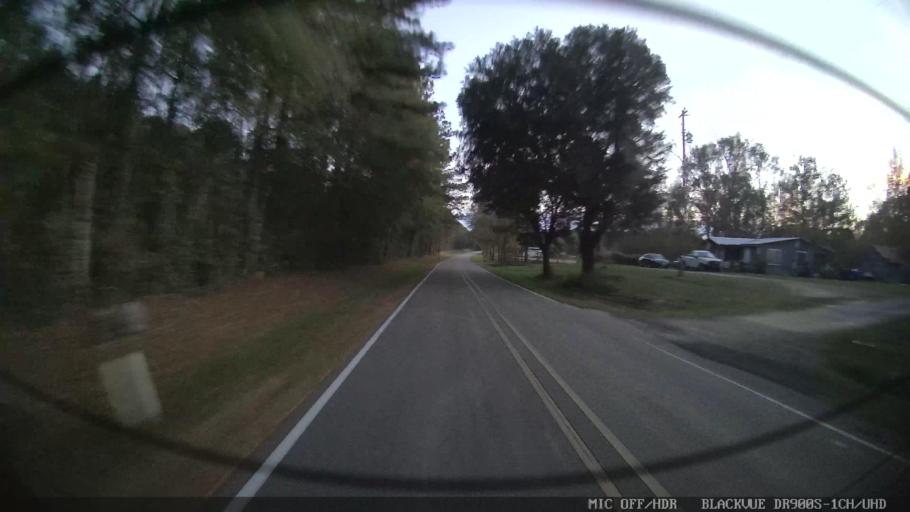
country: US
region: Mississippi
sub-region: Perry County
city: New Augusta
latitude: 31.0914
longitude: -89.1884
